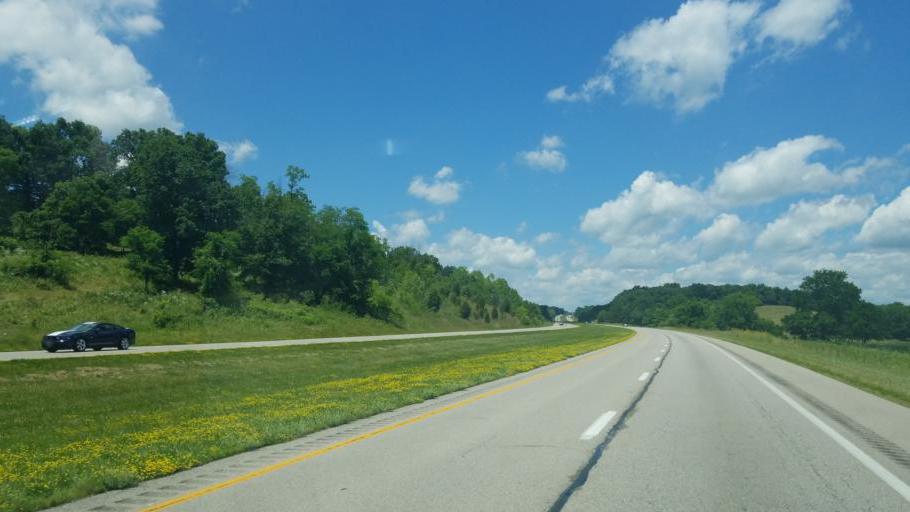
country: US
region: Ohio
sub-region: Gallia County
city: Gallipolis
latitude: 38.8621
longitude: -82.2562
